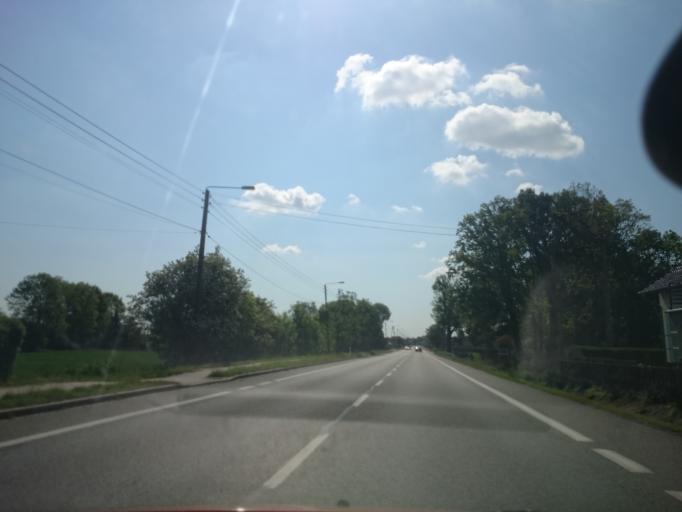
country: PL
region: Opole Voivodeship
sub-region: Powiat opolski
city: Naklo
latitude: 50.5857
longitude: 18.1056
